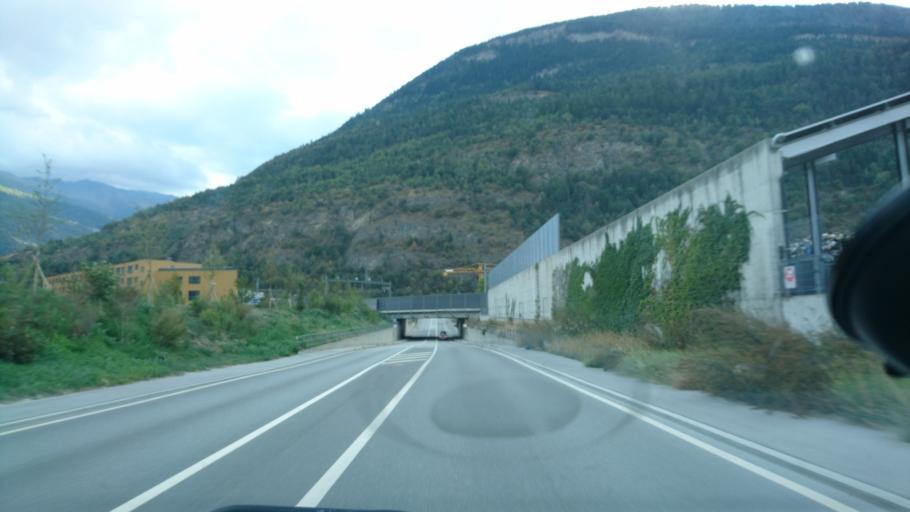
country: CH
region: Valais
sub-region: Visp District
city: Baltschieder
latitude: 46.2996
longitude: 7.8664
